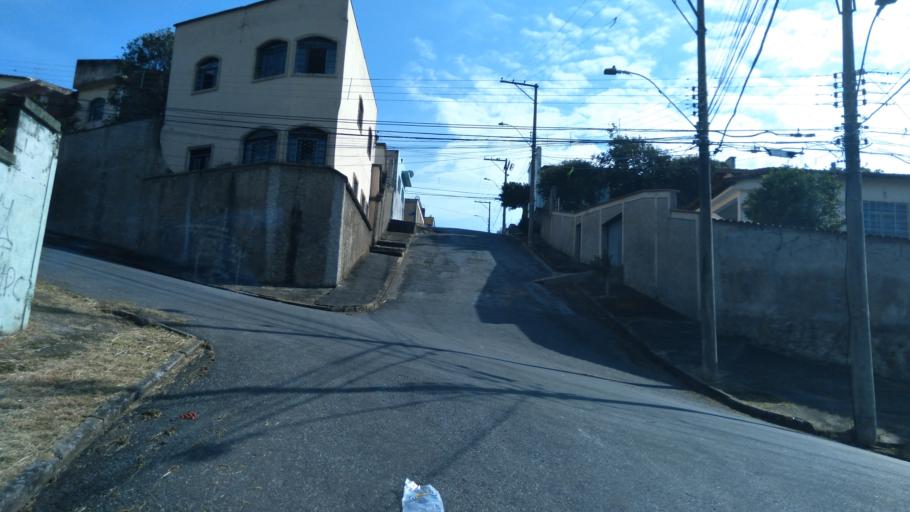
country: BR
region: Minas Gerais
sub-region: Belo Horizonte
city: Belo Horizonte
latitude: -19.8963
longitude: -43.9420
